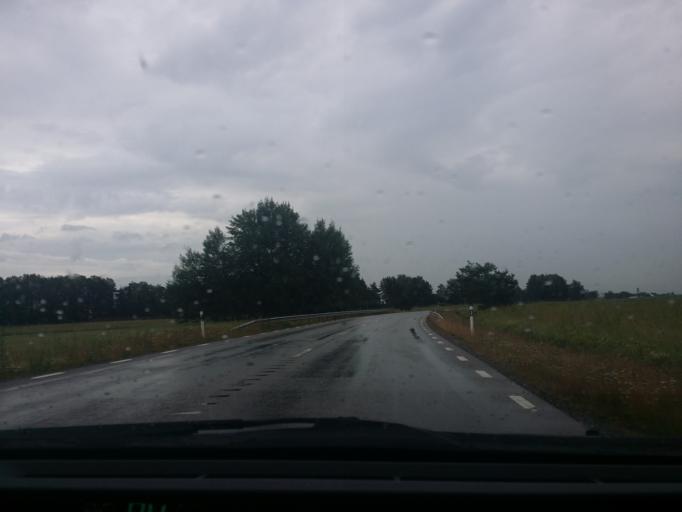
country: SE
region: OErebro
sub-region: Lindesbergs Kommun
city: Fellingsbro
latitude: 59.4697
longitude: 15.5394
